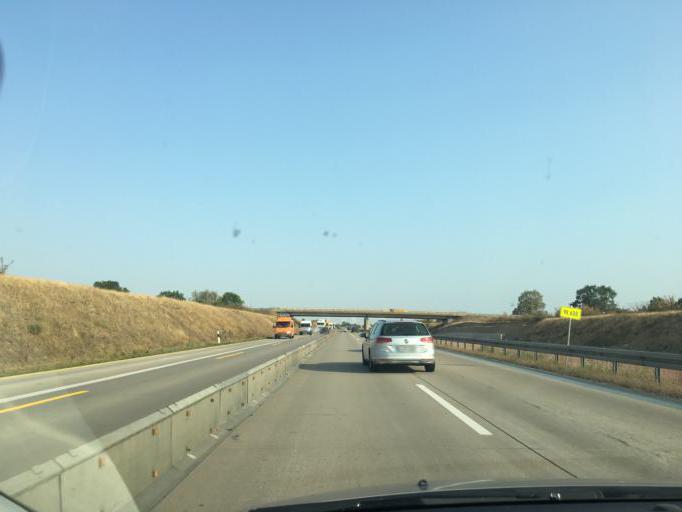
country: DE
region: Saxony-Anhalt
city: Brehna
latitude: 51.5898
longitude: 12.1862
